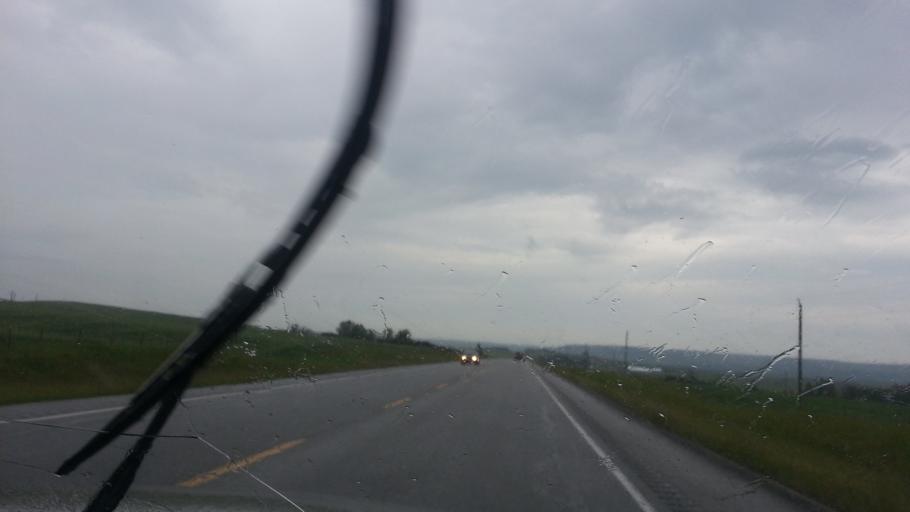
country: CA
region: Alberta
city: Cochrane
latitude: 51.1213
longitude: -114.4666
